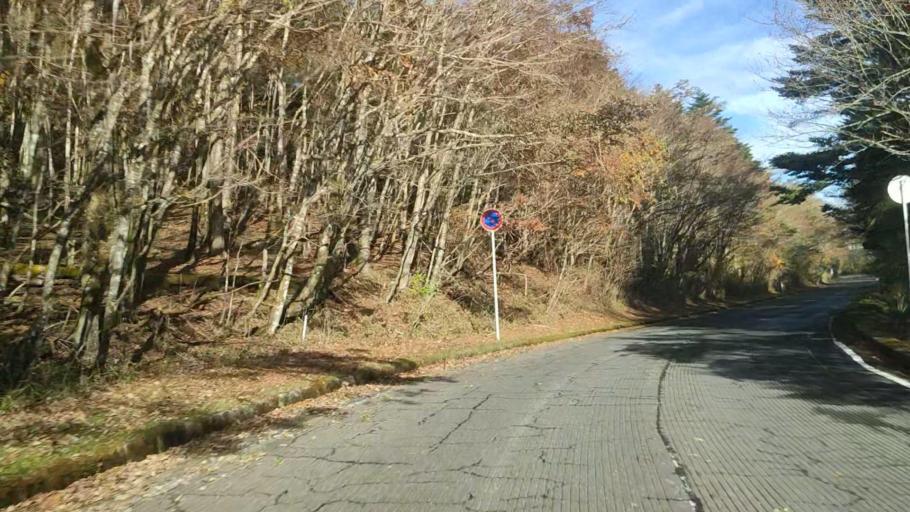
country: JP
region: Shizuoka
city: Fuji
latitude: 35.3034
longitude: 138.7572
